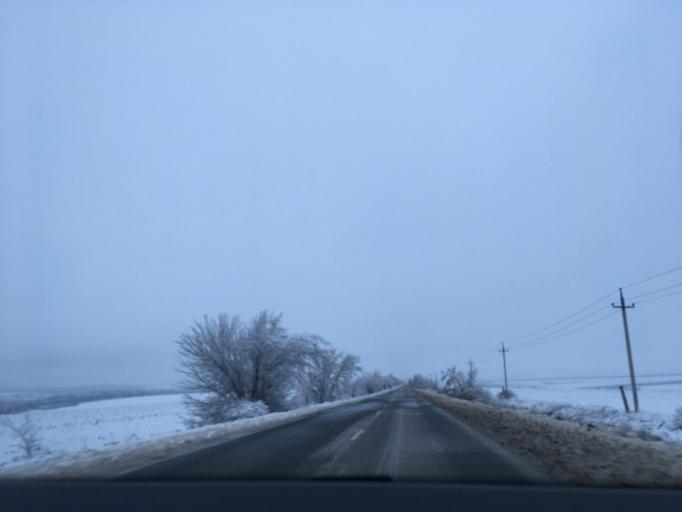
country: RU
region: Voronezj
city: Verkhniy Mamon
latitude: 50.0224
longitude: 40.0888
